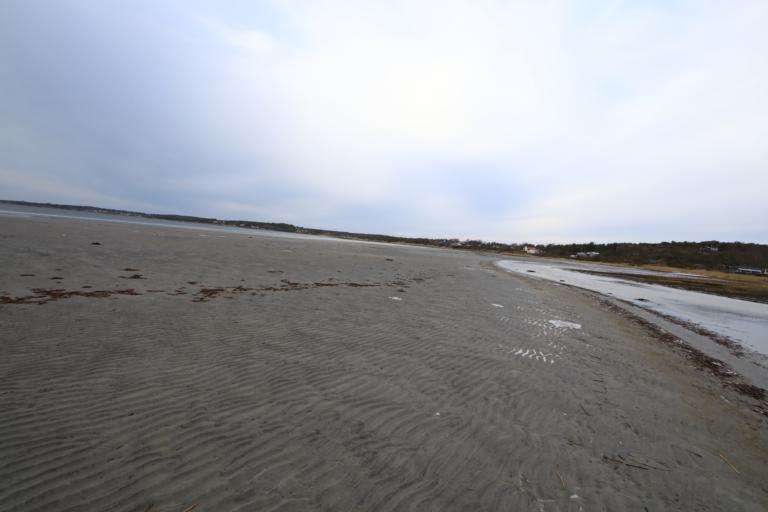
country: SE
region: Halland
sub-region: Varbergs Kommun
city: Varberg
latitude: 57.1823
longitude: 12.2125
